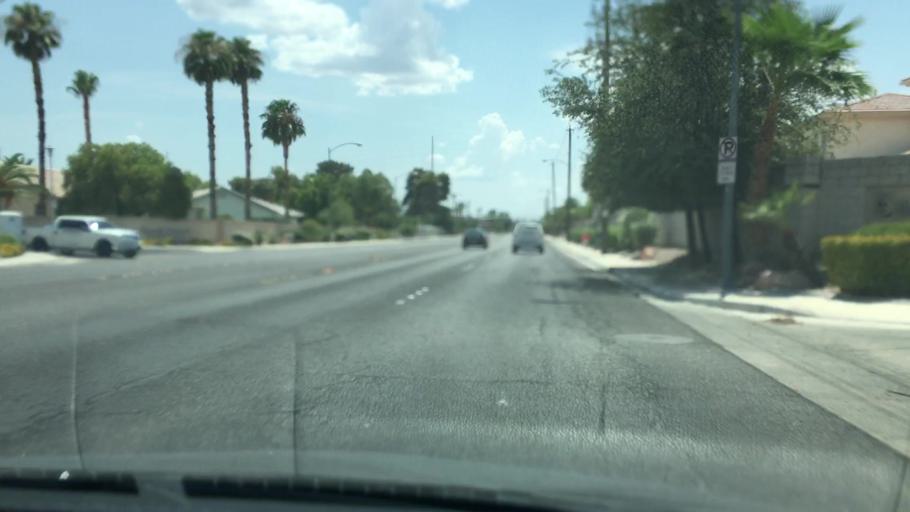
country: US
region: Nevada
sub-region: Clark County
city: Whitney
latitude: 36.0816
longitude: -115.0916
